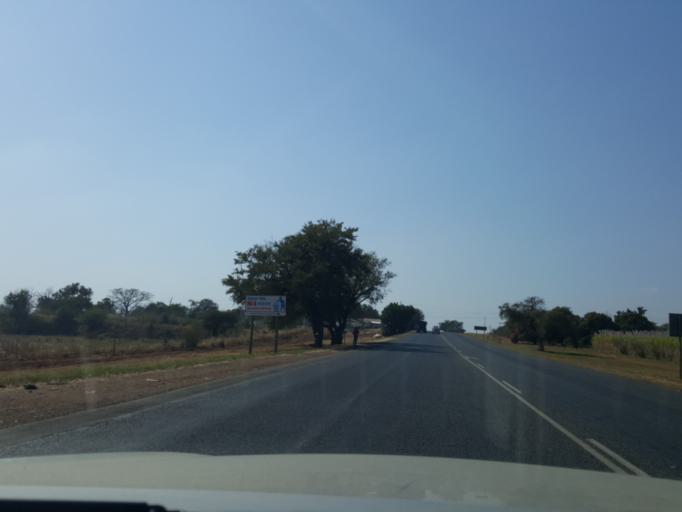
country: SZ
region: Hhohho
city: Ntfonjeni
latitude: -25.4944
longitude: 31.5200
